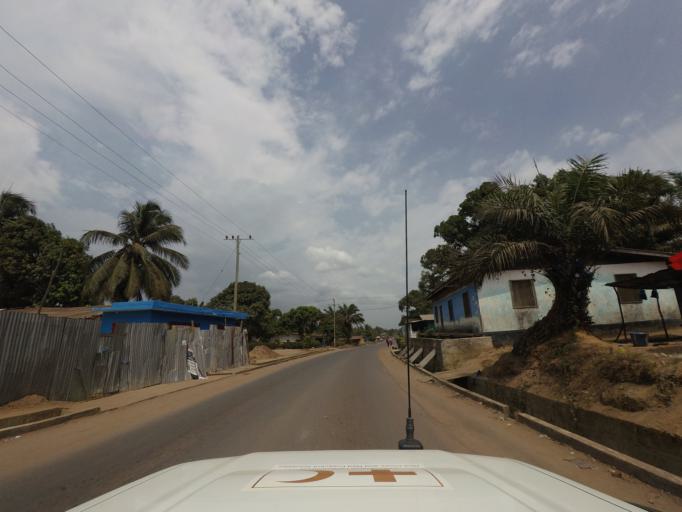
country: LR
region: Montserrado
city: Monrovia
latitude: 6.2845
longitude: -10.6890
